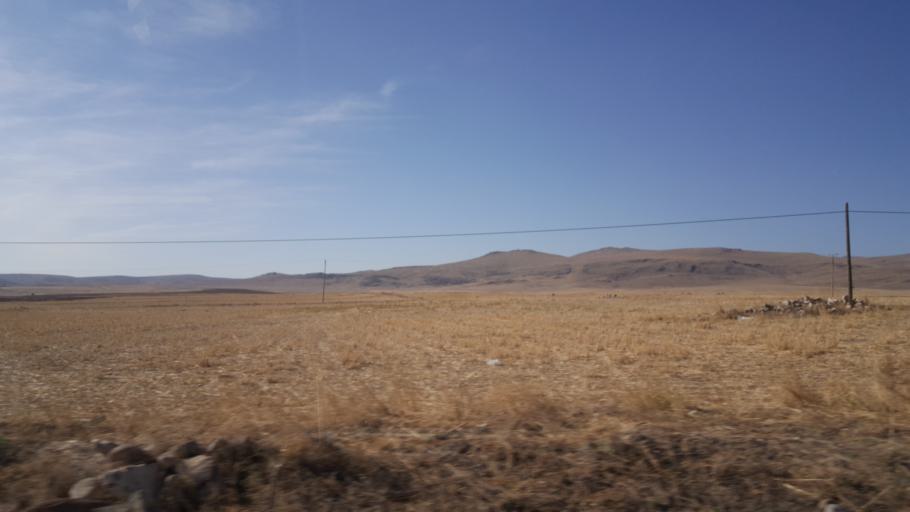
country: TR
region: Ankara
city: Altpinar
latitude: 39.2540
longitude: 32.7525
